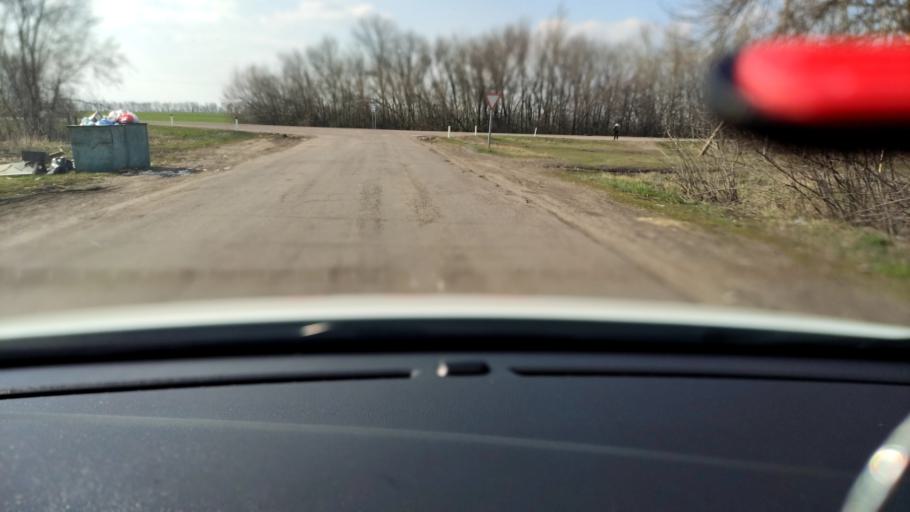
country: RU
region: Voronezj
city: Uryv-Pokrovka
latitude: 51.1470
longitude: 39.0604
